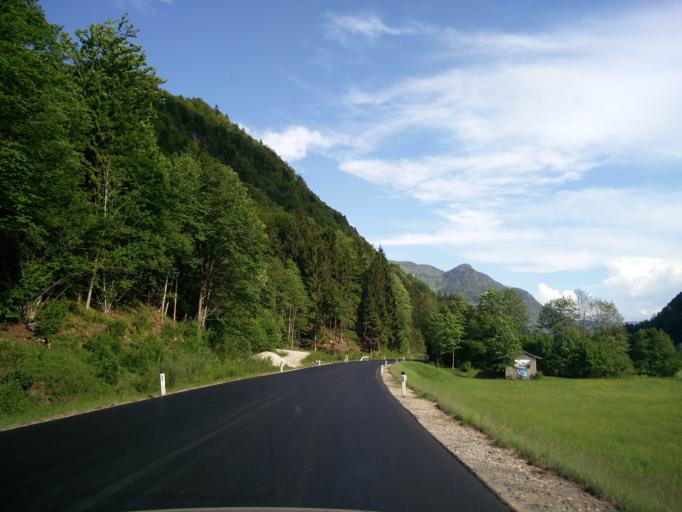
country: DE
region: Bavaria
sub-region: Upper Bavaria
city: Reit im Winkl
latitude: 47.6441
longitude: 12.4509
